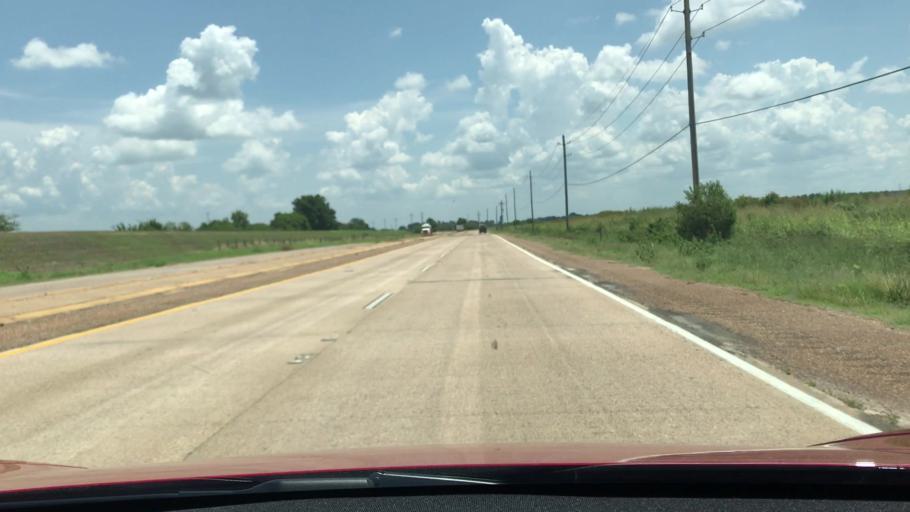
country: US
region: Louisiana
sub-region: Bossier Parish
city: Bossier City
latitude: 32.3936
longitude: -93.6869
